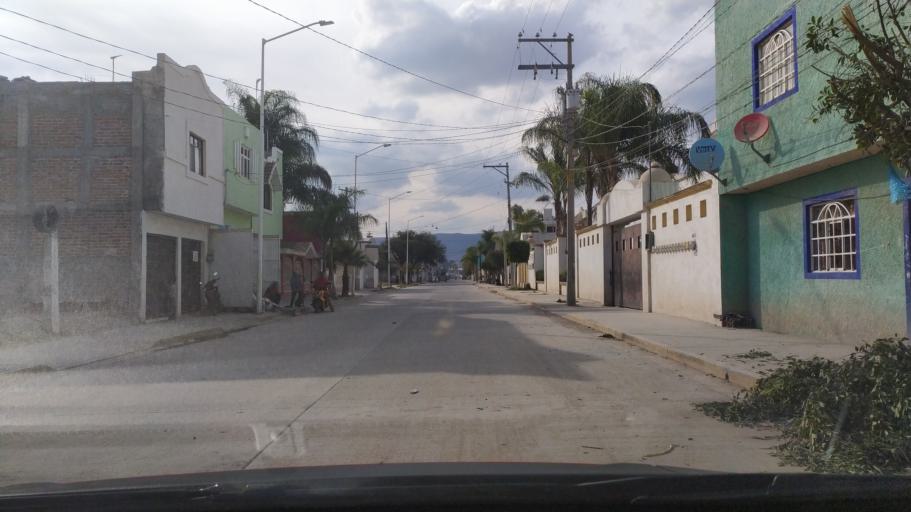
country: MX
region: Guanajuato
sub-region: San Francisco del Rincon
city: Fraccionamiento la Mezquitera
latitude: 21.0054
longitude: -101.8482
